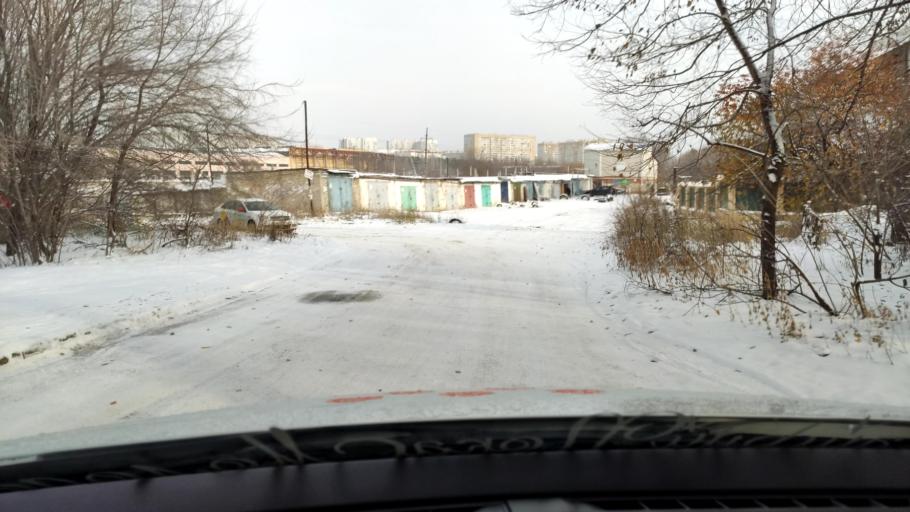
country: RU
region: Voronezj
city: Voronezh
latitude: 51.6827
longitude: 39.1385
